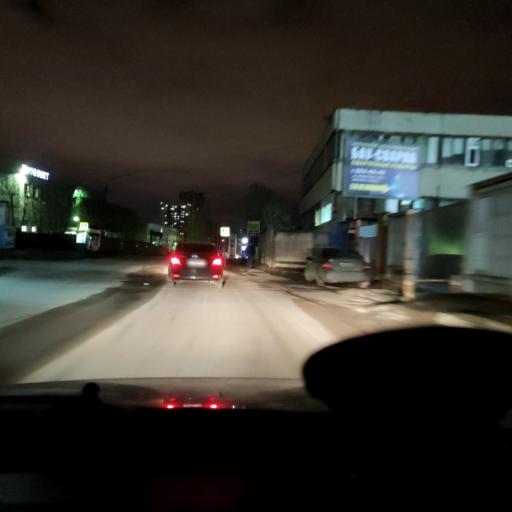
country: RU
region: Perm
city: Kondratovo
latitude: 57.9697
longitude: 56.1778
